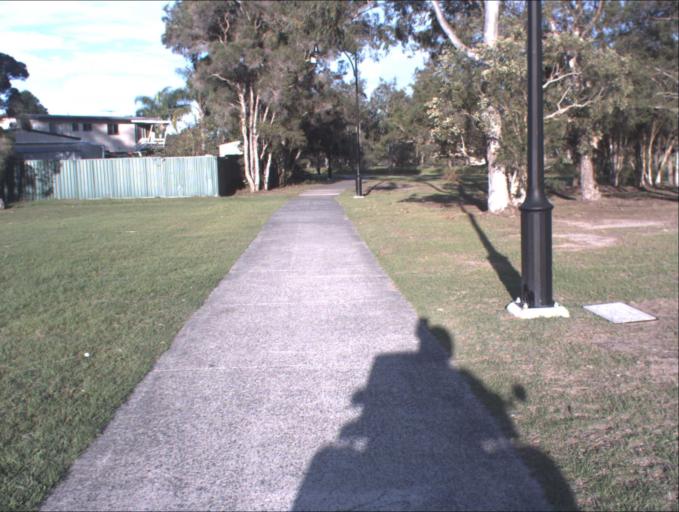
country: AU
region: Queensland
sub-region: Logan
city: Logan Reserve
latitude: -27.6913
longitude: 153.0874
